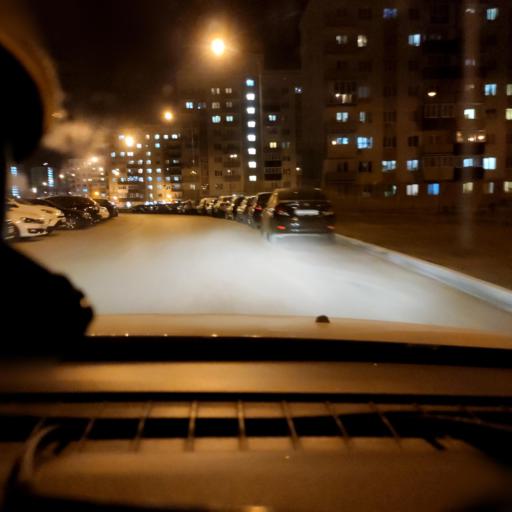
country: RU
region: Samara
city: Samara
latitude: 53.1114
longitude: 50.1466
